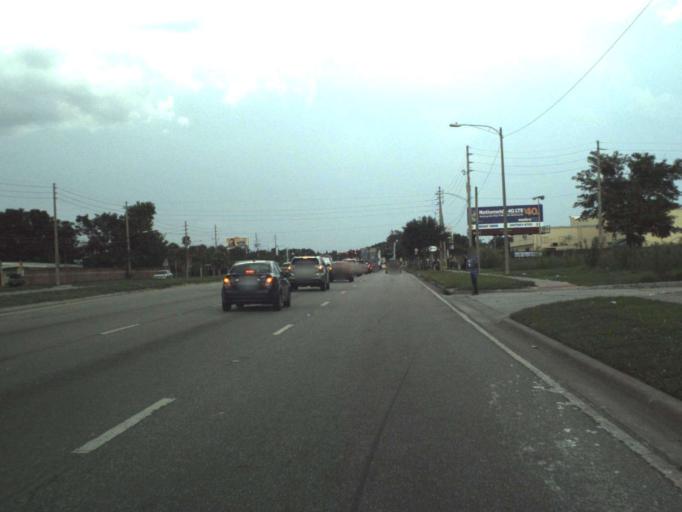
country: US
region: Florida
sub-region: Orange County
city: Orlando
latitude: 28.5490
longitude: -81.4136
